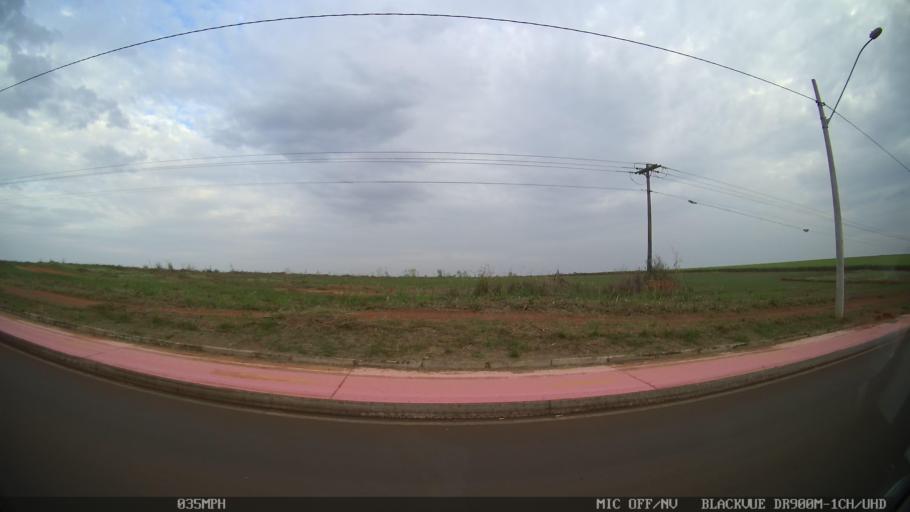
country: BR
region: Sao Paulo
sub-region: Americana
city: Americana
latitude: -22.6517
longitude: -47.3305
